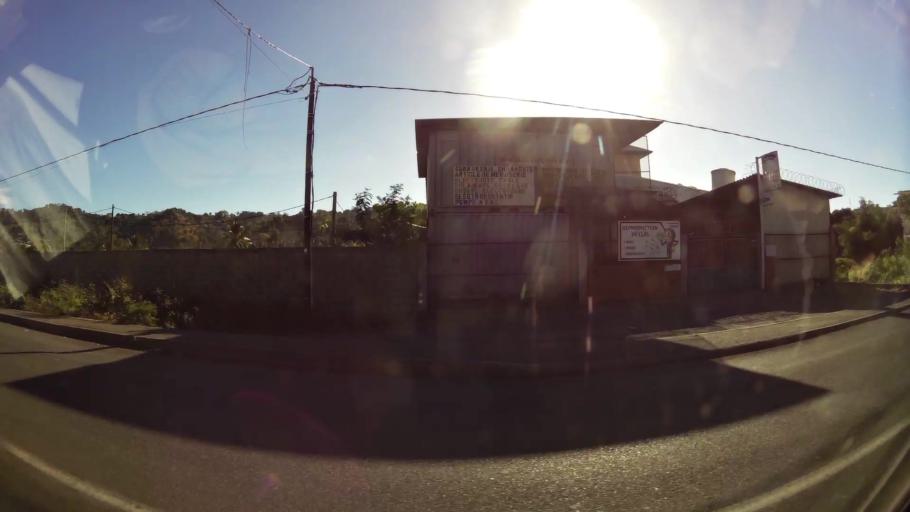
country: YT
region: Mamoudzou
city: Mamoudzou
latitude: -12.7665
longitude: 45.2249
